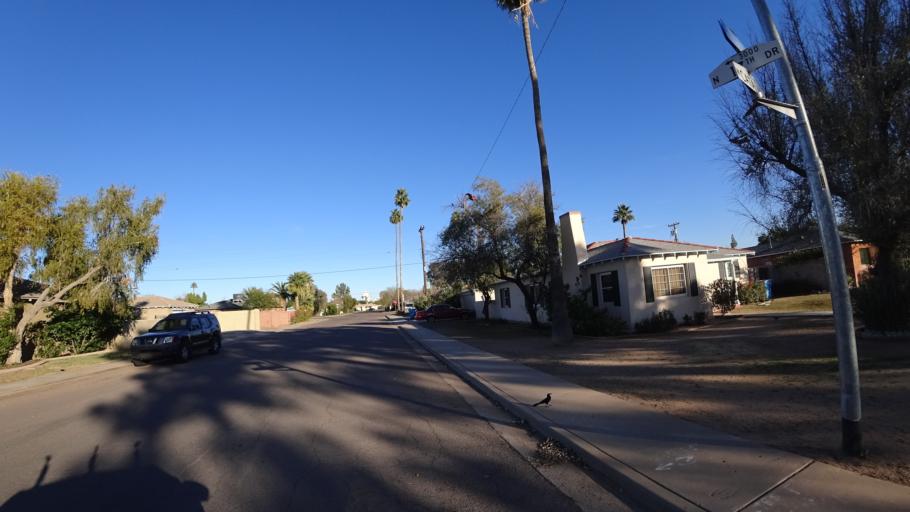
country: US
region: Arizona
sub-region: Maricopa County
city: Phoenix
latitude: 33.4823
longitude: -112.0967
